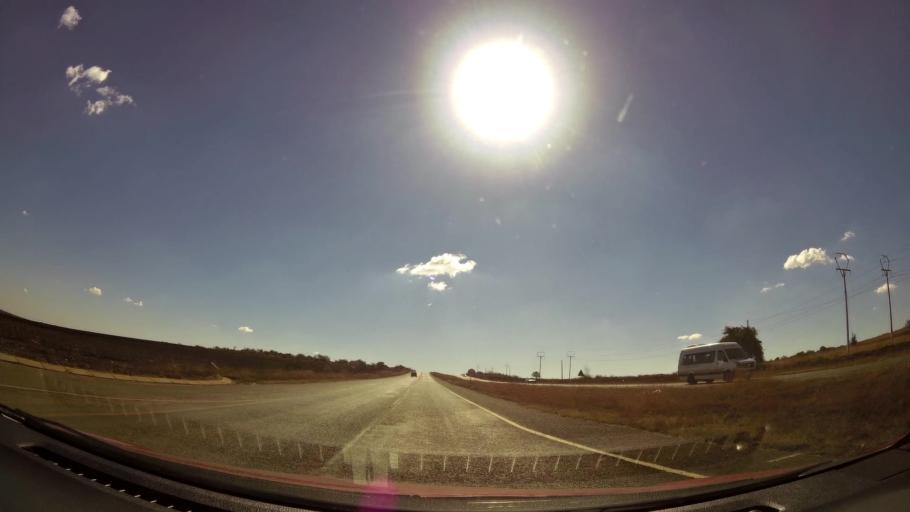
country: ZA
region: Gauteng
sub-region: West Rand District Municipality
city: Carletonville
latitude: -26.3915
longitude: 27.4175
